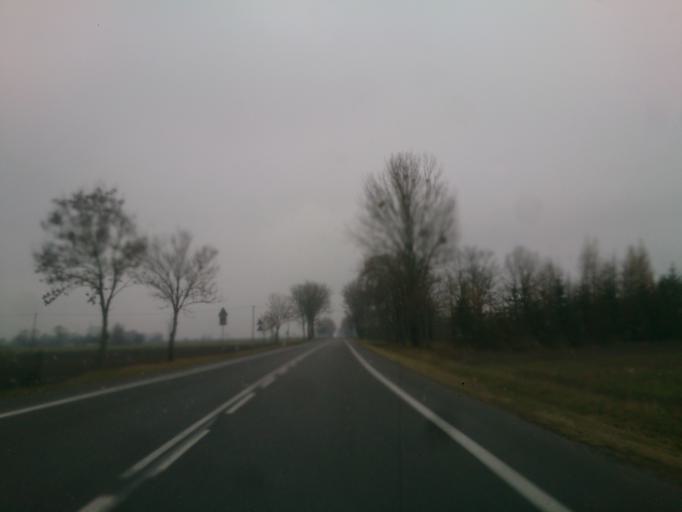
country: PL
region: Masovian Voivodeship
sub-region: Powiat plocki
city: Drobin
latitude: 52.7197
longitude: 20.0185
